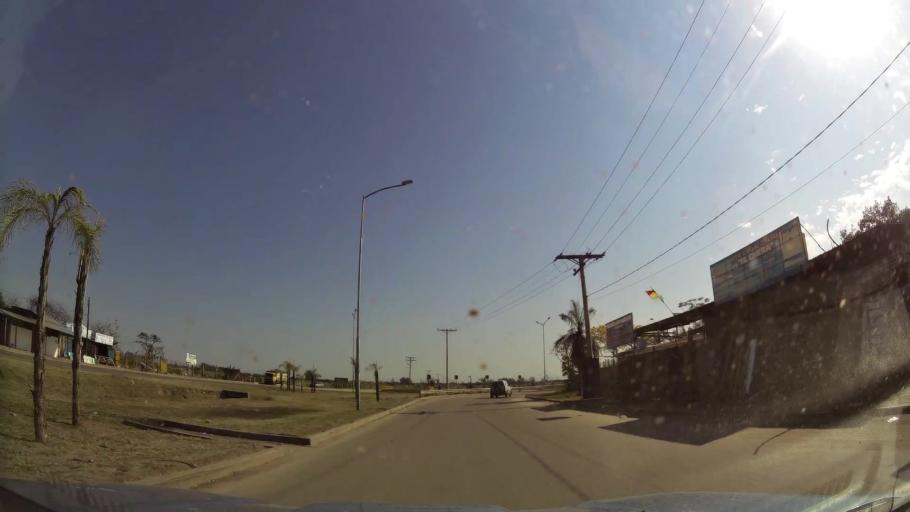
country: BO
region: Santa Cruz
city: Santa Cruz de la Sierra
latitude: -17.8288
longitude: -63.1394
